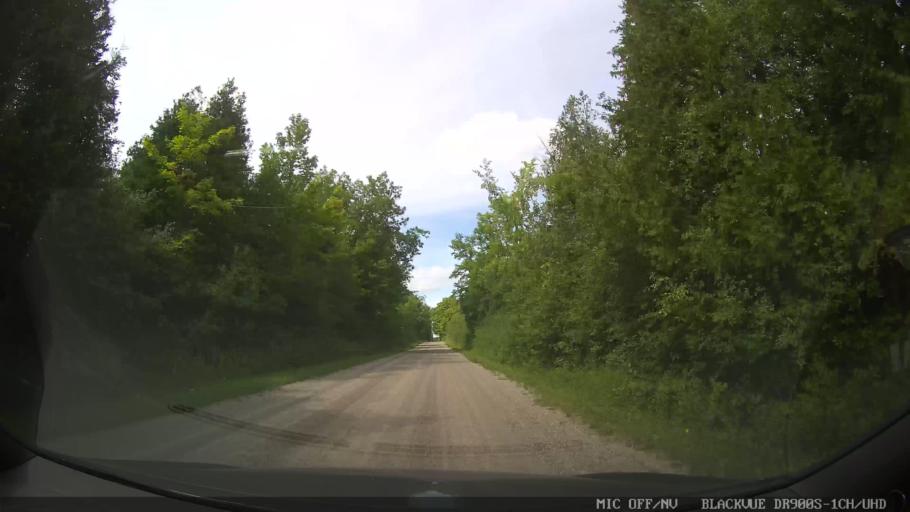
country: CA
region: Ontario
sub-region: Lanark County
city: Smiths Falls
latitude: 44.9289
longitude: -75.8786
